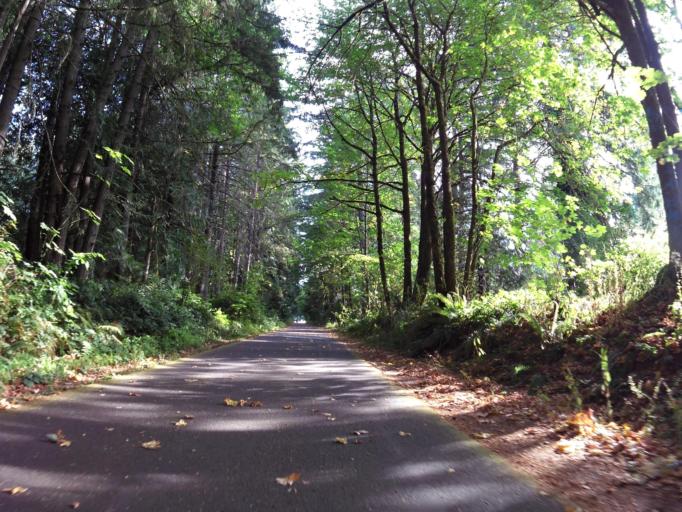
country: US
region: Washington
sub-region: Thurston County
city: Lacey
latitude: 47.0000
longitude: -122.8337
